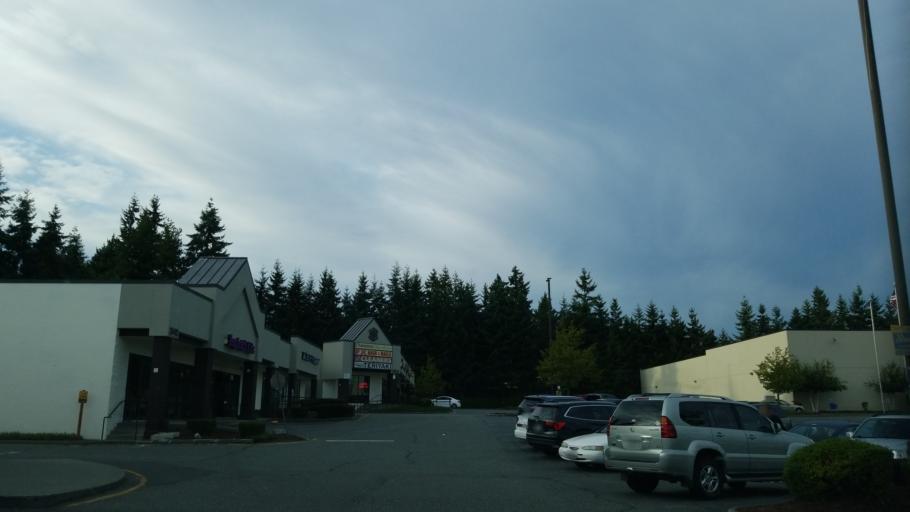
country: US
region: Washington
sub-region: Snohomish County
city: Lynnwood
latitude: 47.8227
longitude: -122.3163
